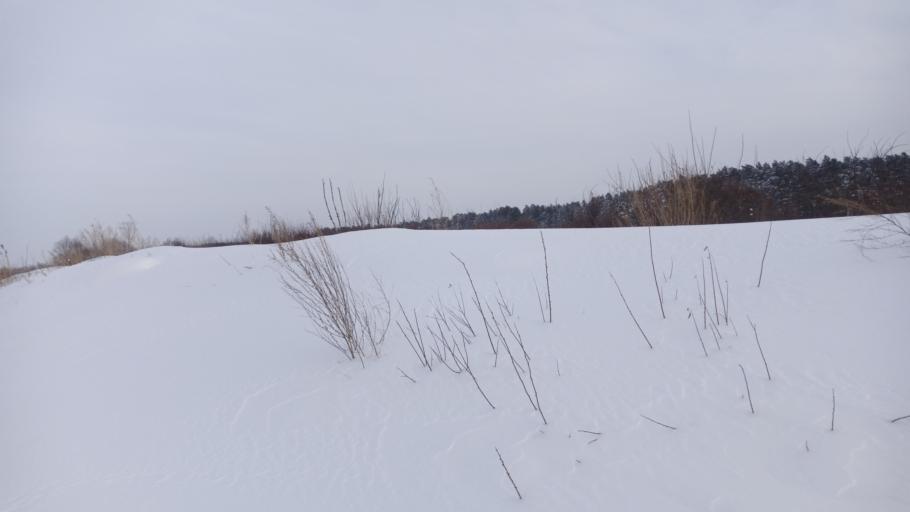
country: RU
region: Altai Krai
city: Yuzhnyy
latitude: 53.3080
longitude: 83.7210
